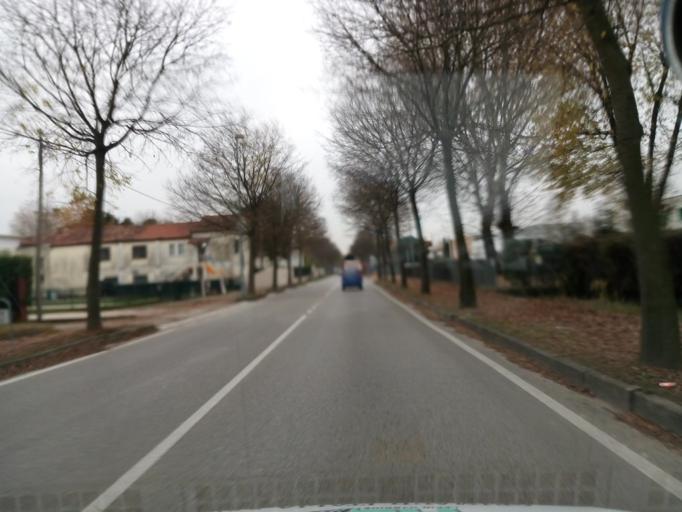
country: IT
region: Veneto
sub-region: Provincia di Padova
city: Vigonza
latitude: 45.4351
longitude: 11.9594
